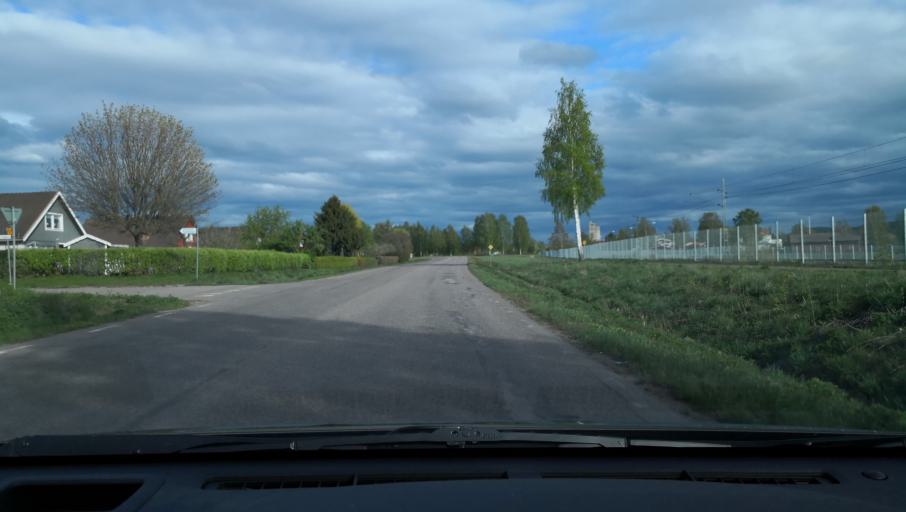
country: SE
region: Dalarna
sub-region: Hedemora Kommun
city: Hedemora
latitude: 60.2808
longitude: 15.9659
